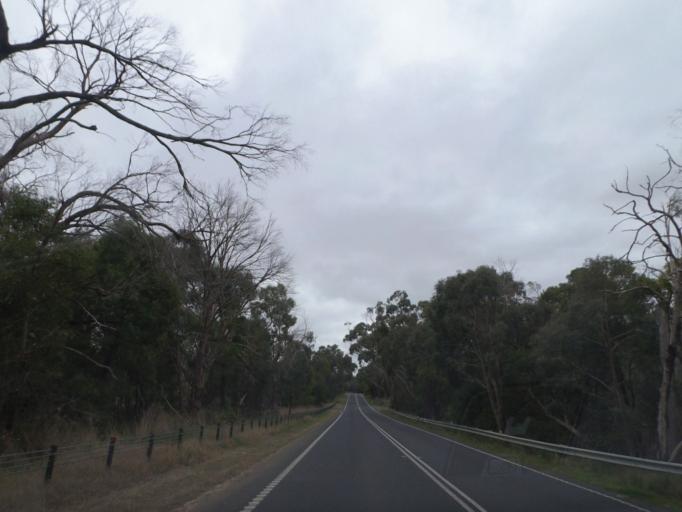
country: AU
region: Victoria
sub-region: Whittlesea
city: Whittlesea
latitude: -37.3838
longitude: 145.0296
